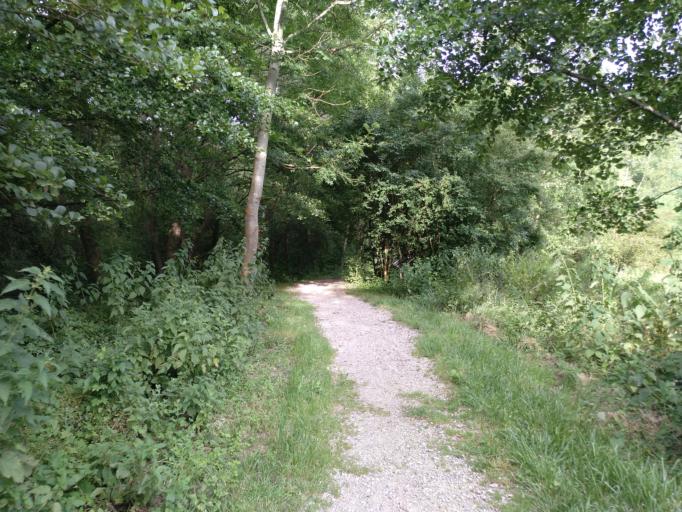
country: FR
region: Rhone-Alpes
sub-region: Departement du Rhone
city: Marennes
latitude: 45.6333
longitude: 4.9232
